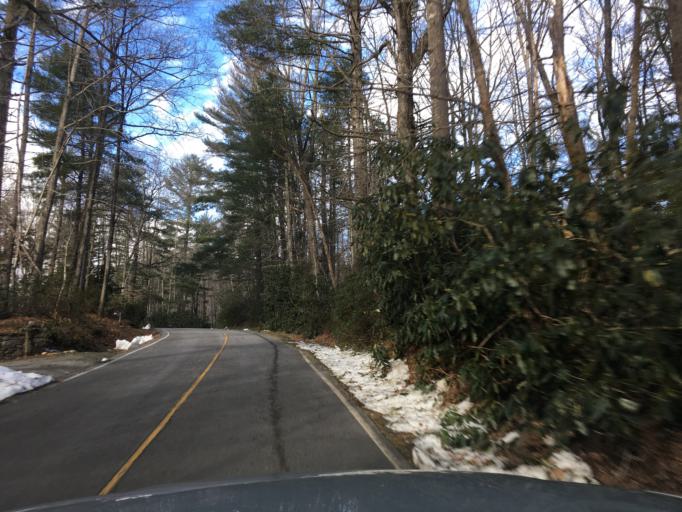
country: US
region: North Carolina
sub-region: Jackson County
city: Cullowhee
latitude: 35.1228
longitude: -83.0114
